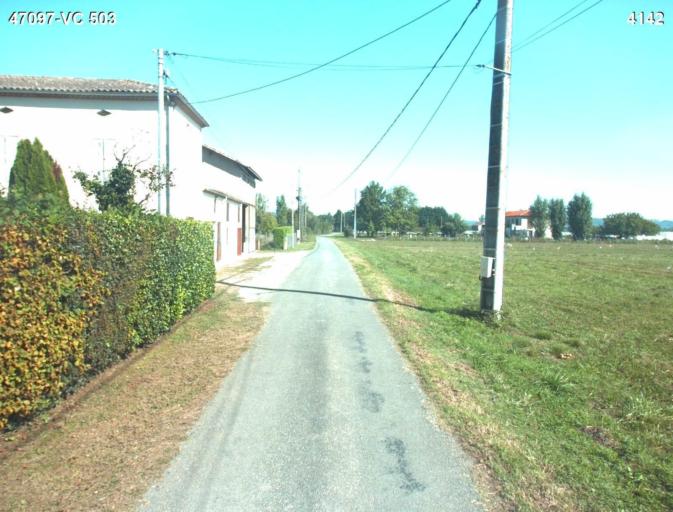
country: FR
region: Aquitaine
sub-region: Departement du Lot-et-Garonne
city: Port-Sainte-Marie
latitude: 44.2223
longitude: 0.3804
